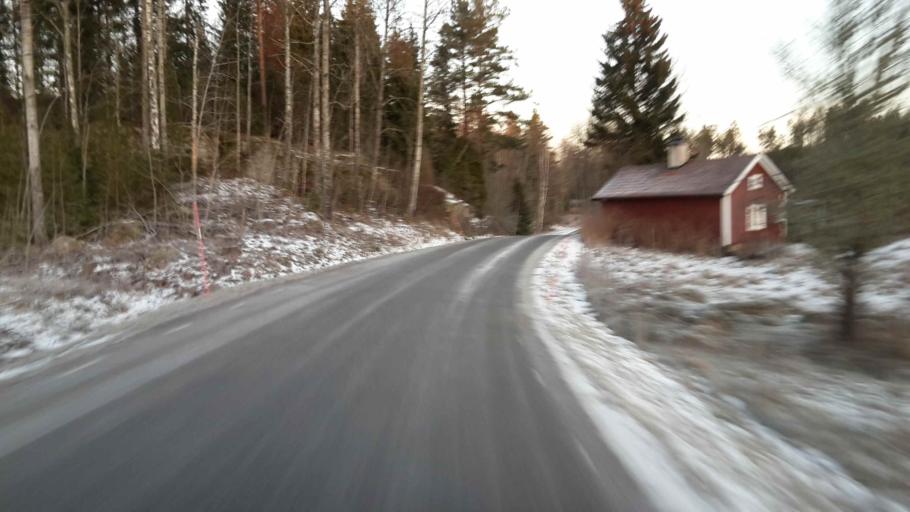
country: SE
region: OEstergoetland
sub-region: Atvidabergs Kommun
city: Atvidaberg
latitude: 58.2557
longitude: 16.1014
